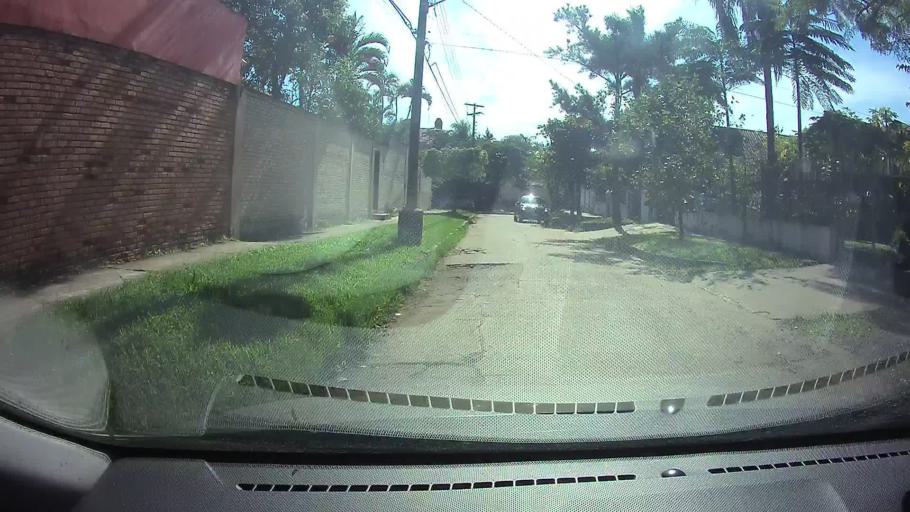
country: PY
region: Central
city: Fernando de la Mora
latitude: -25.2830
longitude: -57.5427
